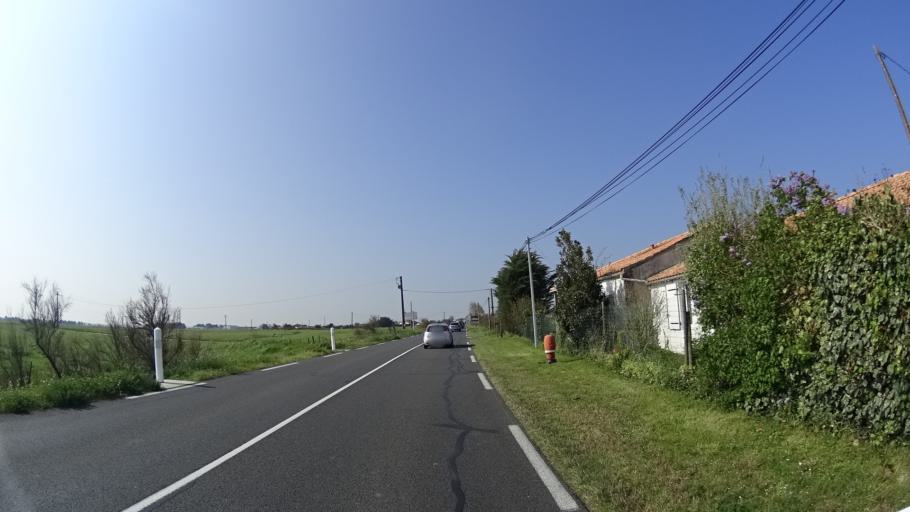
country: FR
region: Pays de la Loire
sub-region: Departement de la Vendee
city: Bouin
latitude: 46.9806
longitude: -1.9846
